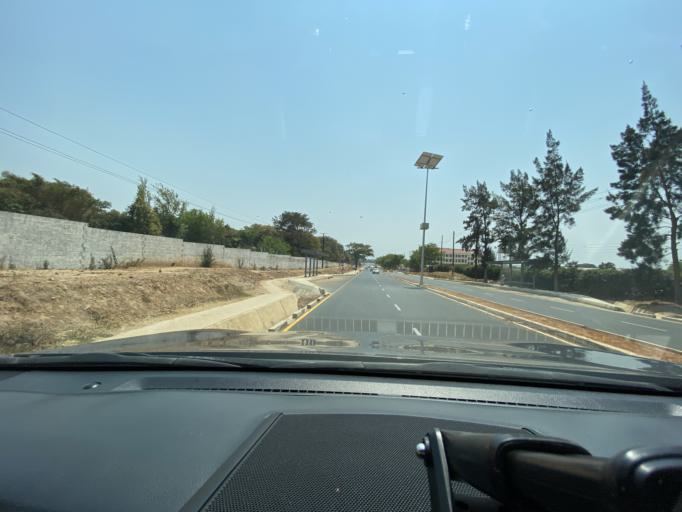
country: ZM
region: Lusaka
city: Lusaka
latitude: -15.3663
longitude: 28.3469
